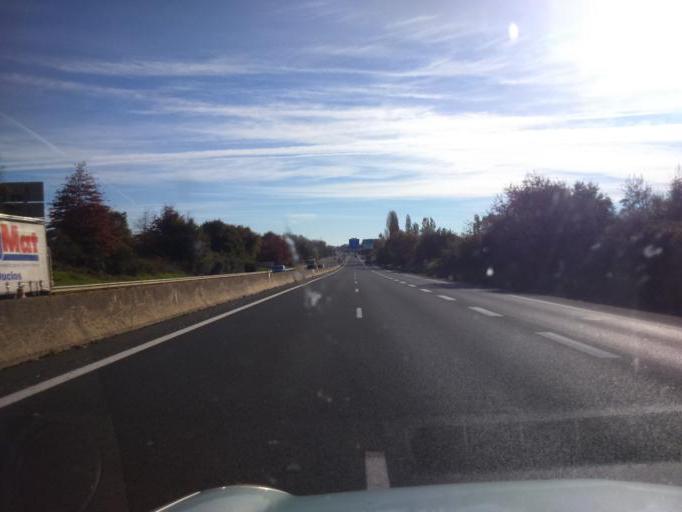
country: FR
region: Poitou-Charentes
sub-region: Departement de la Charente-Maritime
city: Breuil-Magne
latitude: 45.9634
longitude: -0.9646
